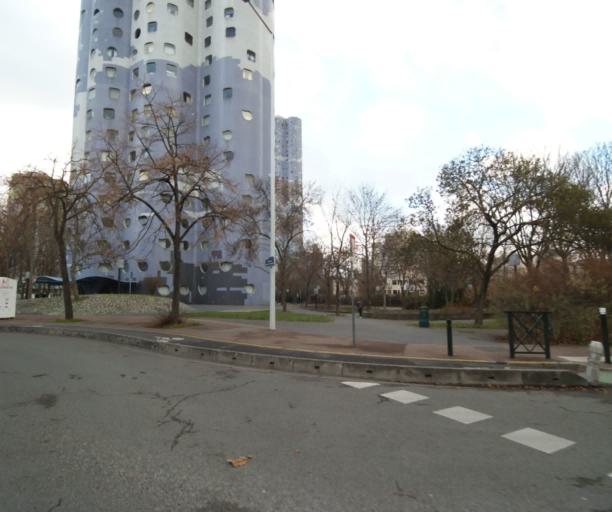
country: FR
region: Ile-de-France
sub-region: Departement des Hauts-de-Seine
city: La Defense
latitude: 48.8900
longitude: 2.2301
